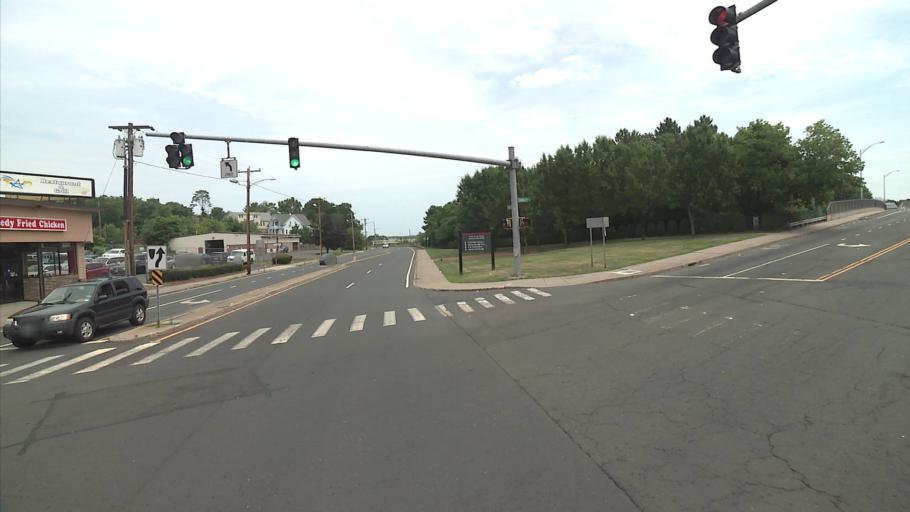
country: US
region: Connecticut
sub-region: Hartford County
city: New Britain
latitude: 41.6738
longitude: -72.7736
